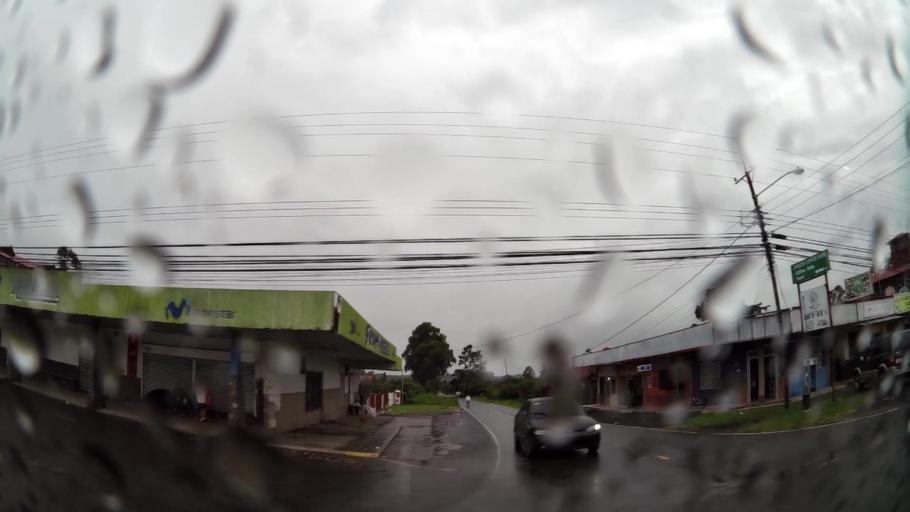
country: PA
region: Chiriqui
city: Volcan
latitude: 8.7807
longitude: -82.6459
